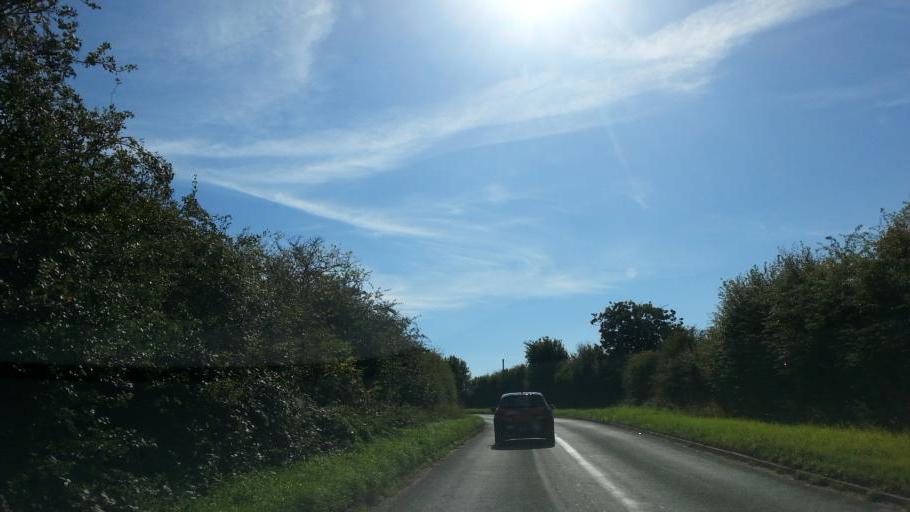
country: GB
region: England
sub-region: Staffordshire
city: Stafford
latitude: 52.7948
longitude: -2.1610
